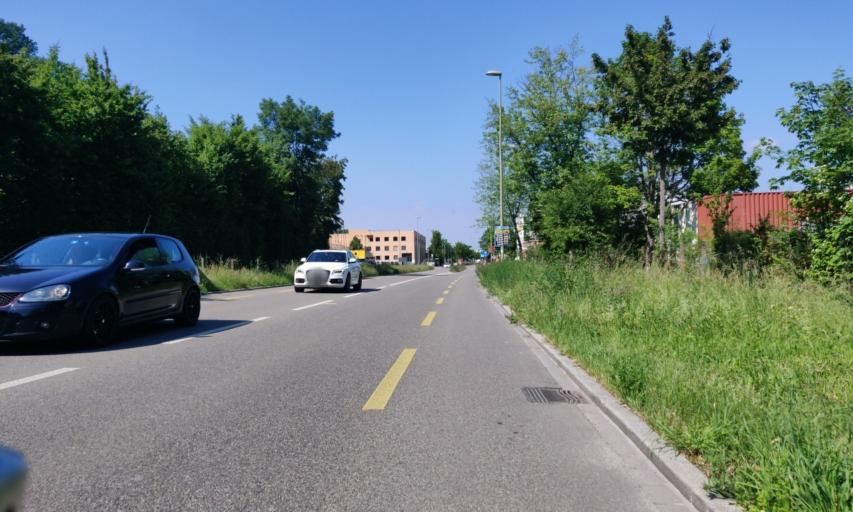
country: CH
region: Basel-Landschaft
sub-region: Bezirk Arlesheim
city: Munchenstein
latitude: 47.5231
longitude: 7.6037
